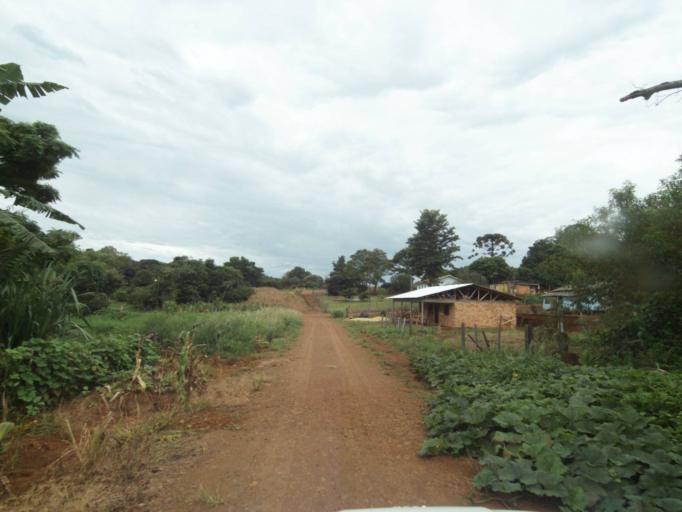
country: BR
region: Parana
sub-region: Guaraniacu
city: Guaraniacu
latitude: -24.9201
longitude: -52.9370
